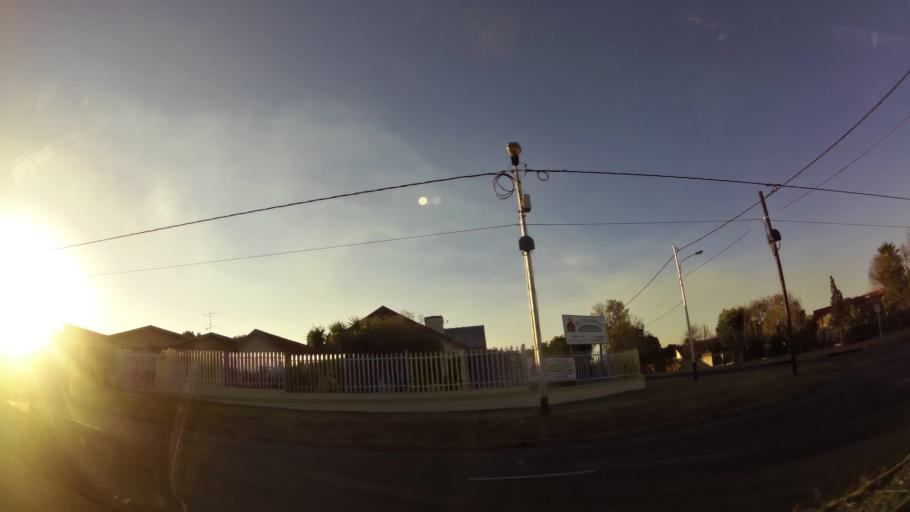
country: ZA
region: Gauteng
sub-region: City of Johannesburg Metropolitan Municipality
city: Roodepoort
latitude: -26.1562
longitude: 27.8811
